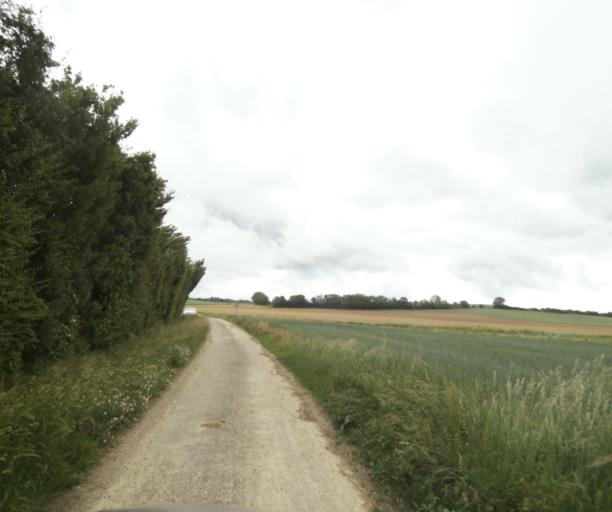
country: FR
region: Rhone-Alpes
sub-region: Departement de l'Ain
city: Miribel
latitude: 45.8457
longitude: 4.9562
